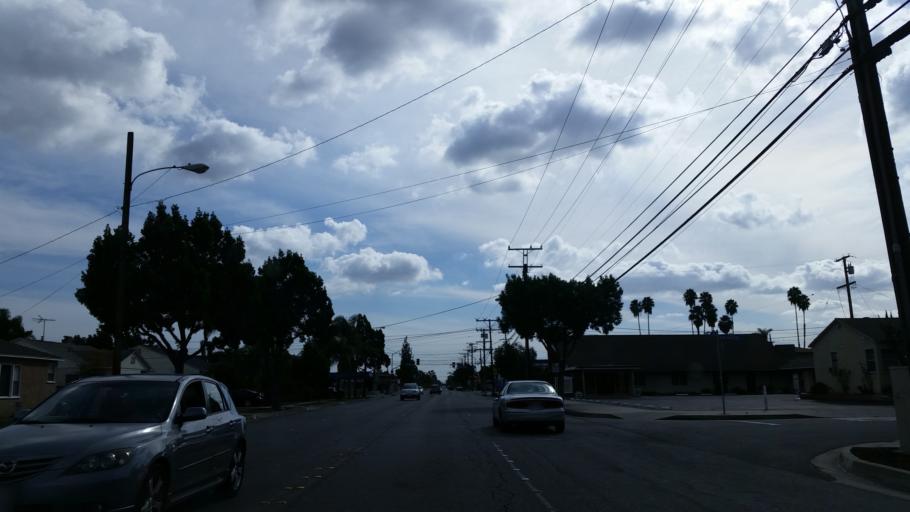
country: US
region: California
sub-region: Los Angeles County
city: Bellflower
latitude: 33.8983
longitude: -118.1341
